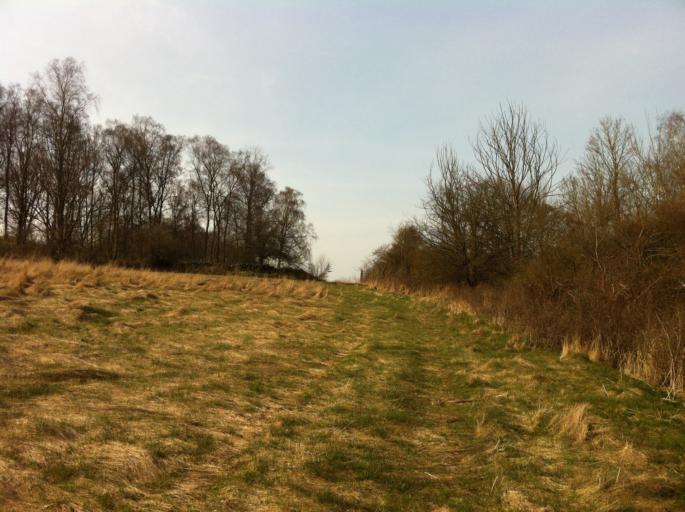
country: SE
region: Skane
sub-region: Eslovs Kommun
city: Stehag
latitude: 56.0146
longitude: 13.3863
